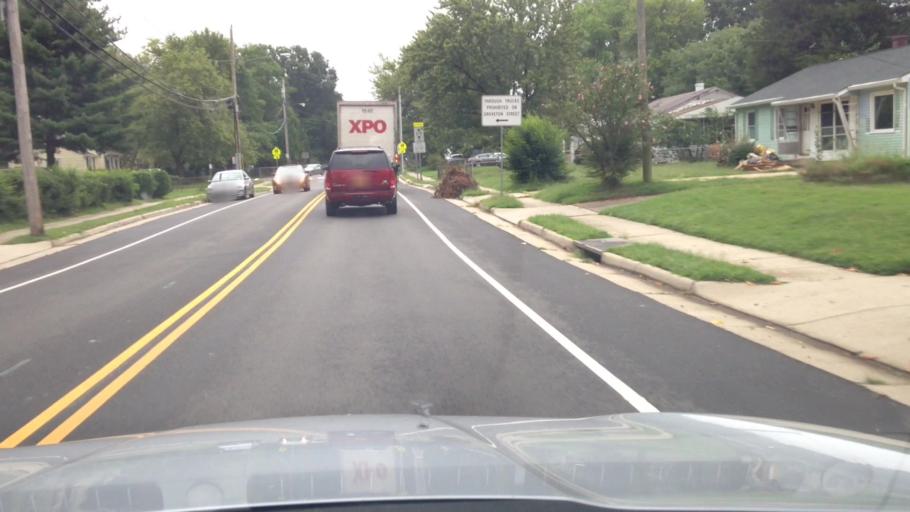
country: US
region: Virginia
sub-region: Fairfax County
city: Groveton
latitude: 38.7711
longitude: -77.0937
